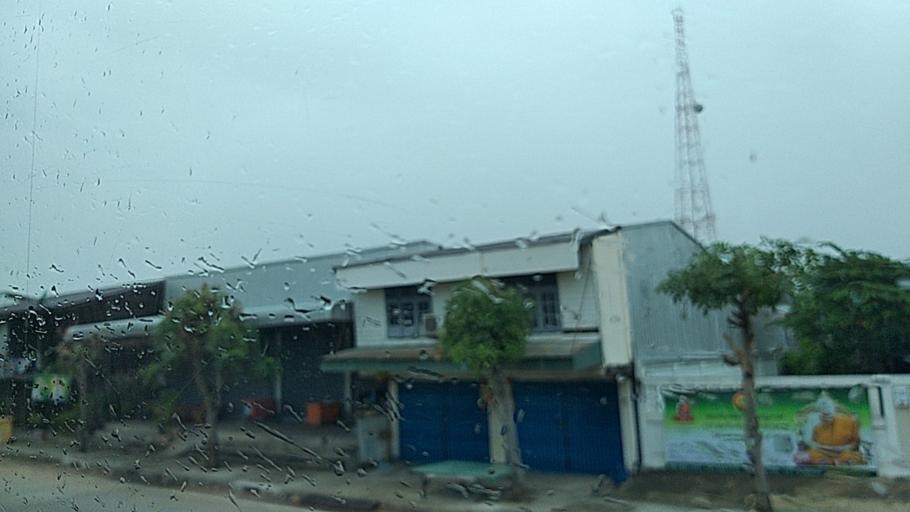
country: TH
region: Maha Sarakham
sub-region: Amphoe Borabue
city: Borabue
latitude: 16.0380
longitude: 103.1226
